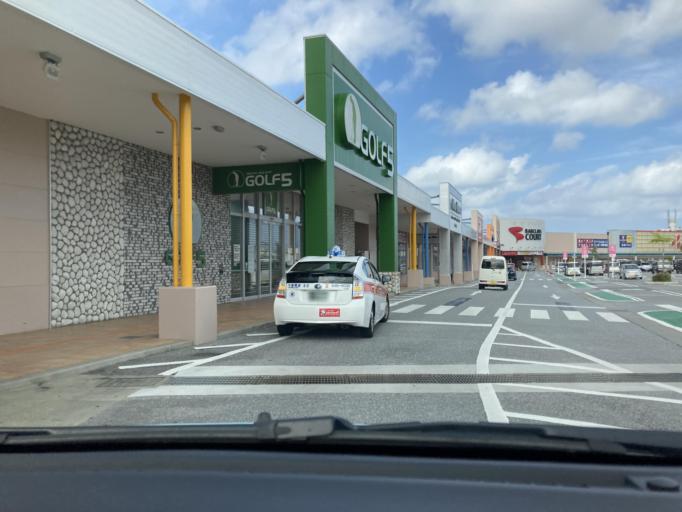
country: JP
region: Okinawa
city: Ginowan
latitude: 26.2520
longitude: 127.7377
